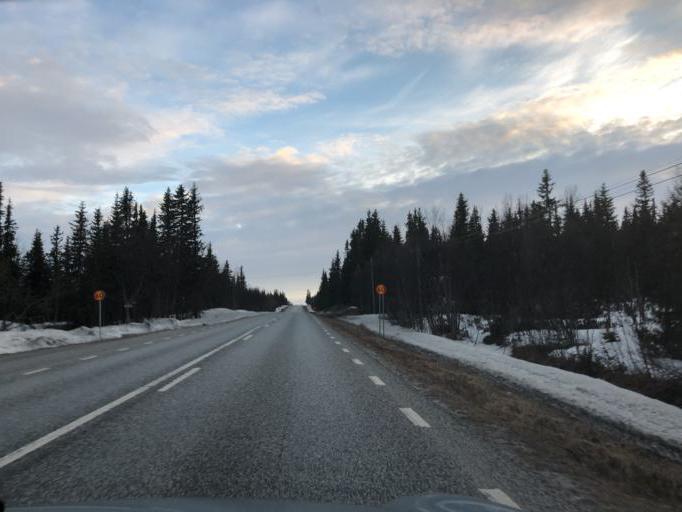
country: NO
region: Hedmark
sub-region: Engerdal
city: Engerdal
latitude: 62.5397
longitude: 12.4363
